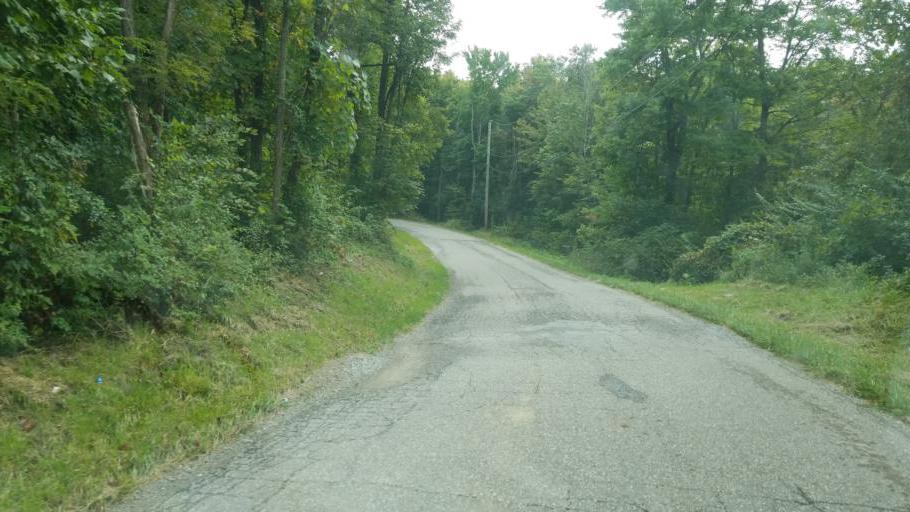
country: US
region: Ohio
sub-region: Jackson County
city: Oak Hill
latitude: 38.9015
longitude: -82.6175
